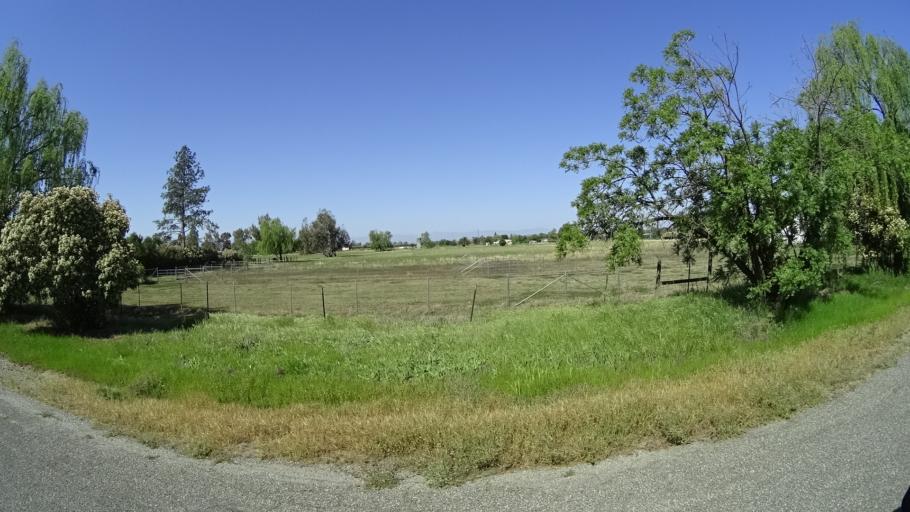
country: US
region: California
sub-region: Glenn County
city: Orland
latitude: 39.7241
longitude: -122.1924
